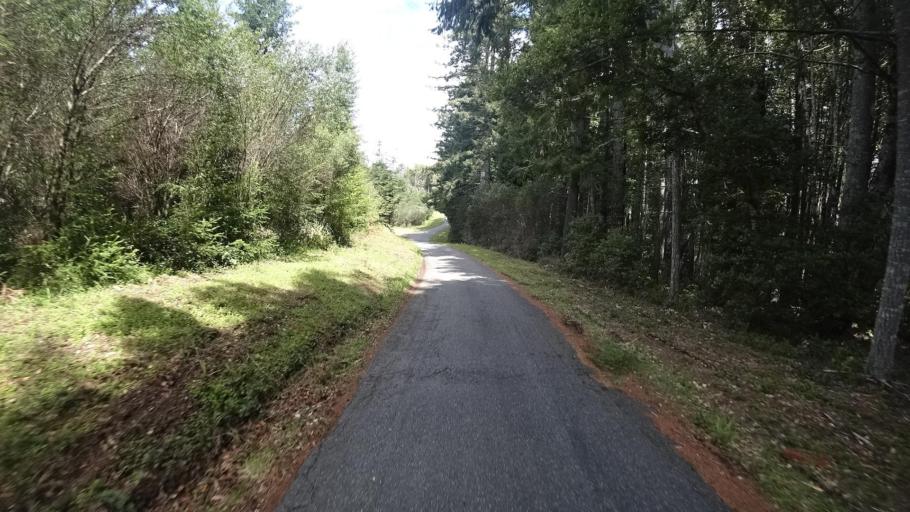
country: US
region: California
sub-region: Humboldt County
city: Blue Lake
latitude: 40.7795
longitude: -123.9627
